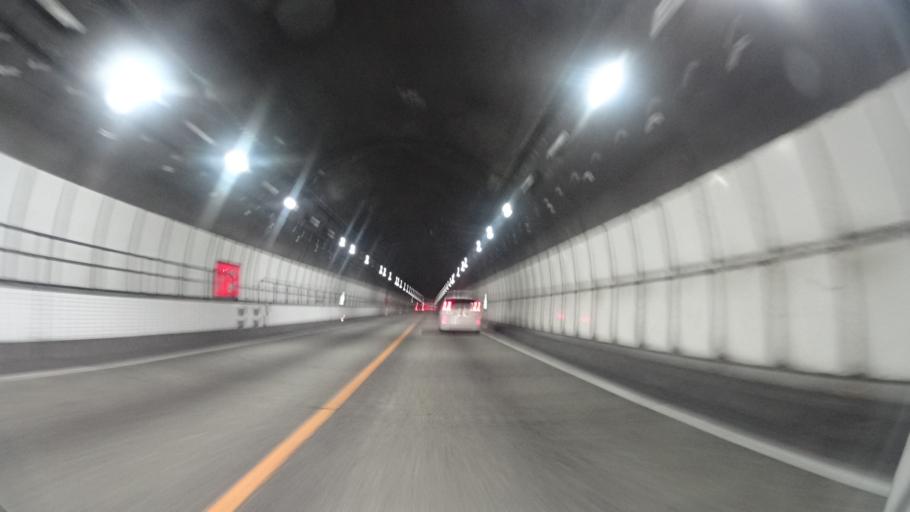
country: JP
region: Osaka
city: Takatsuki
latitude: 34.8737
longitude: 135.6544
